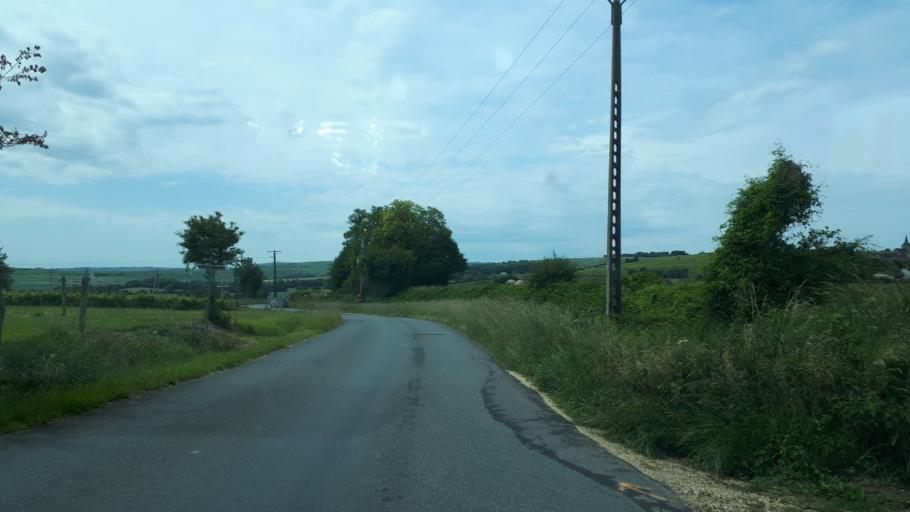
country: FR
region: Centre
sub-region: Departement du Cher
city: Savigny-en-Sancerre
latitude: 47.3978
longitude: 2.8240
